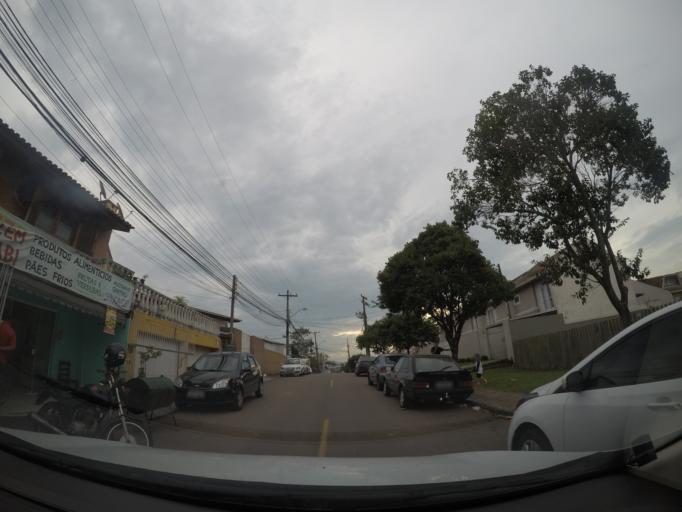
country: BR
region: Parana
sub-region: Curitiba
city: Curitiba
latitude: -25.4645
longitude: -49.2473
